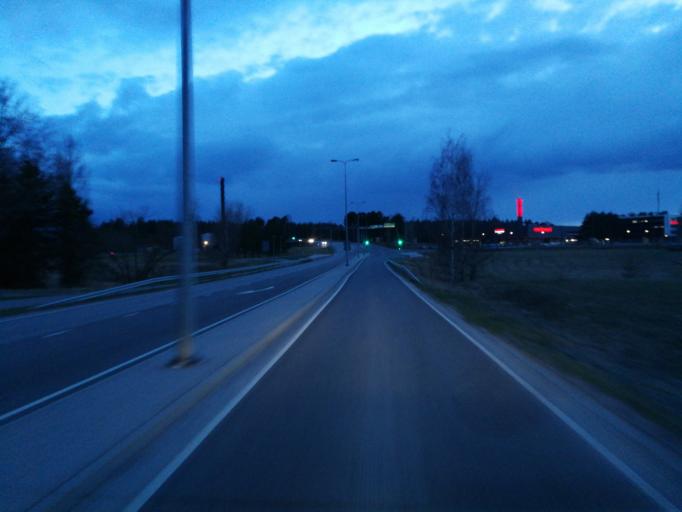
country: FI
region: Varsinais-Suomi
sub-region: Turku
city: Raisio
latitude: 60.4651
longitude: 22.2123
